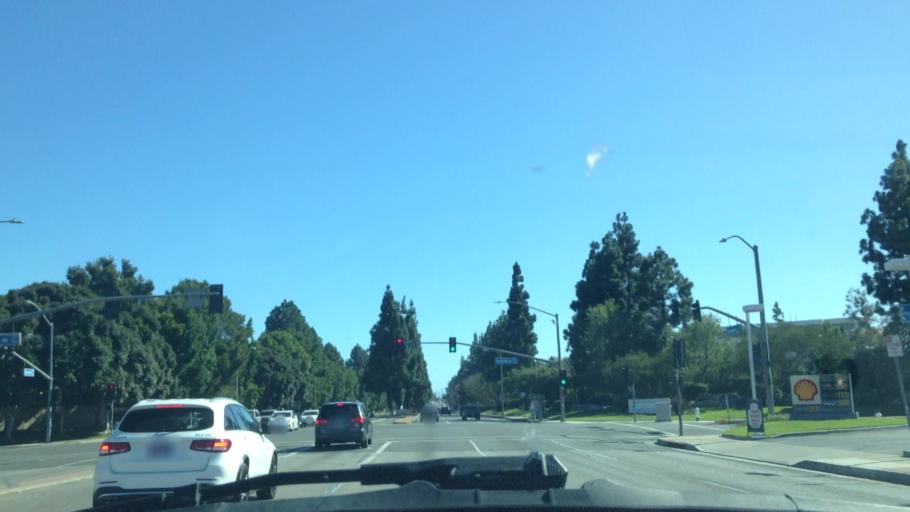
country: US
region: California
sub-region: Orange County
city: Fountain Valley
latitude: 33.6962
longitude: -117.9078
